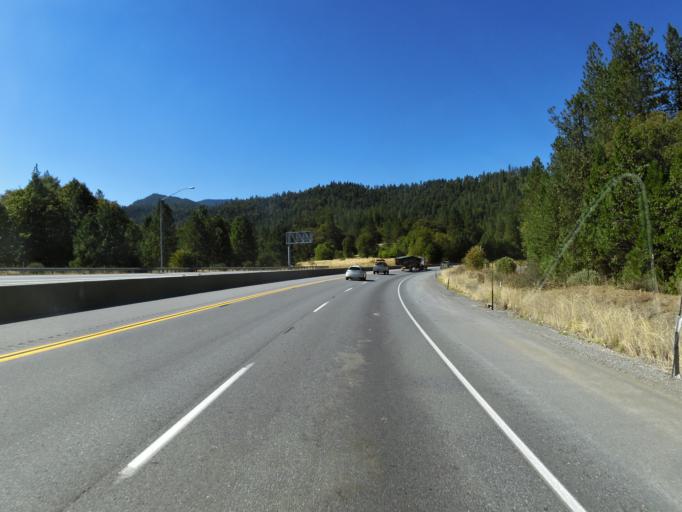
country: US
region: California
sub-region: Shasta County
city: Central Valley (historical)
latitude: 40.9418
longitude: -122.4347
